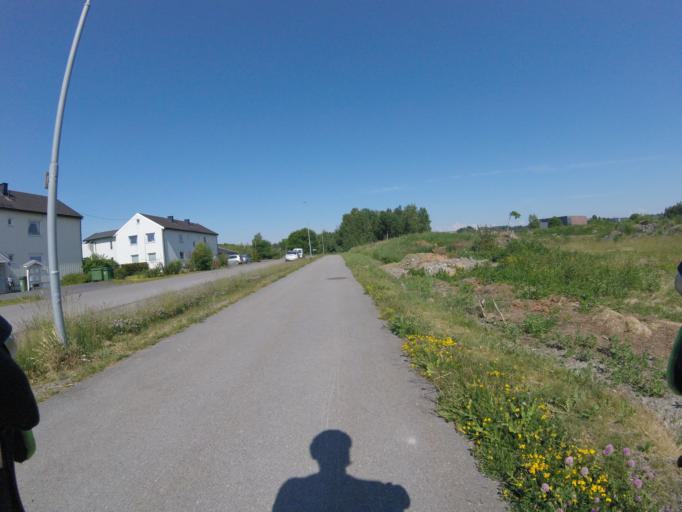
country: NO
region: Akershus
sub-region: Skedsmo
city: Lillestrom
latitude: 59.9659
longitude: 11.0369
